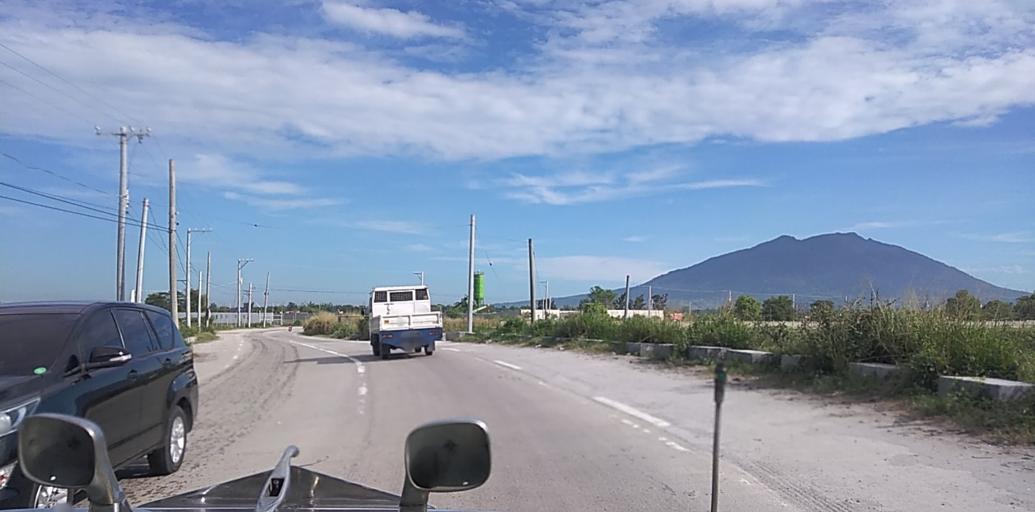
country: PH
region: Central Luzon
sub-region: Province of Pampanga
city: Malino
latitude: 15.1302
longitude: 120.6767
